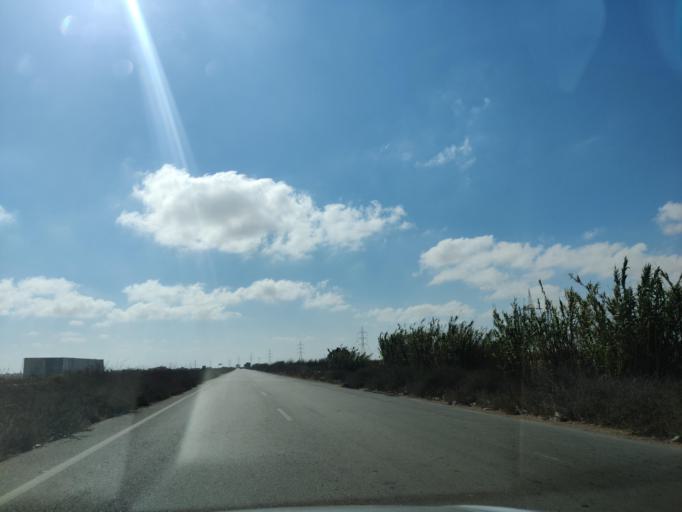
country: EG
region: Muhafazat Matruh
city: Al `Alamayn
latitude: 31.0564
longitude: 28.2521
